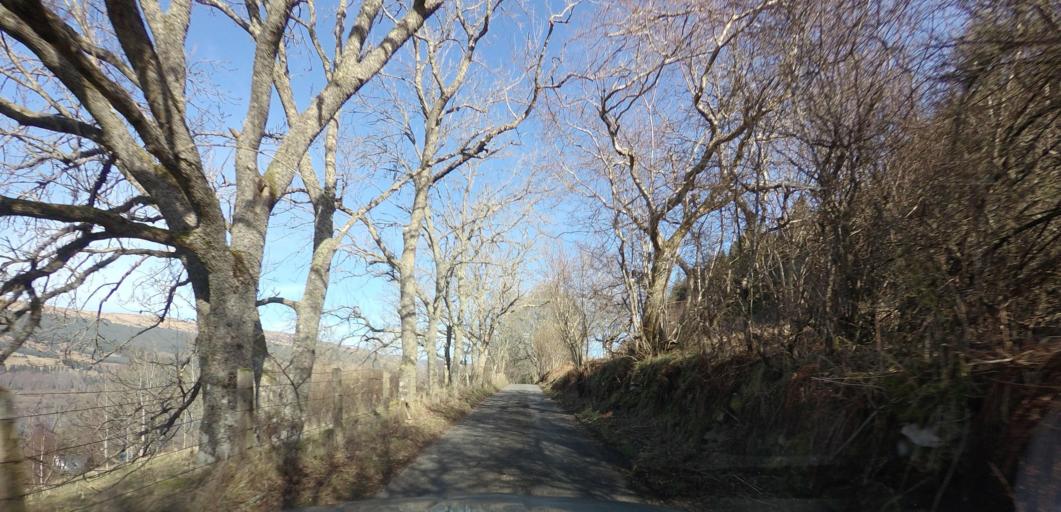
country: GB
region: Scotland
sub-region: Perth and Kinross
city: Comrie
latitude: 56.5464
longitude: -4.0978
